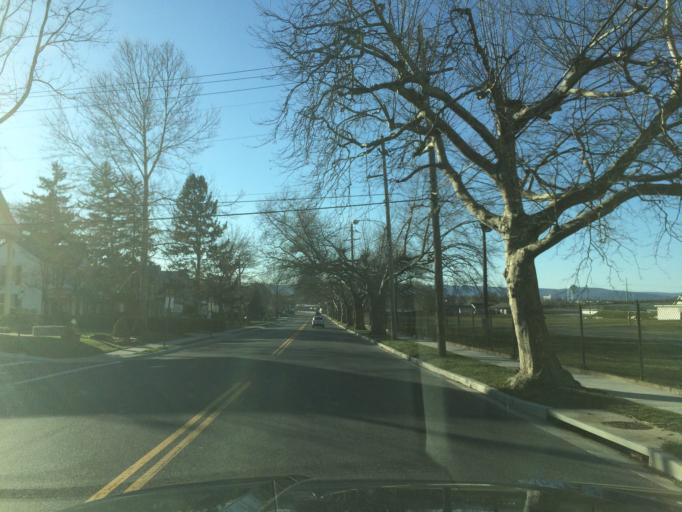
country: US
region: Maryland
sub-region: Frederick County
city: Frederick
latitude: 39.4113
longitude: -77.3956
